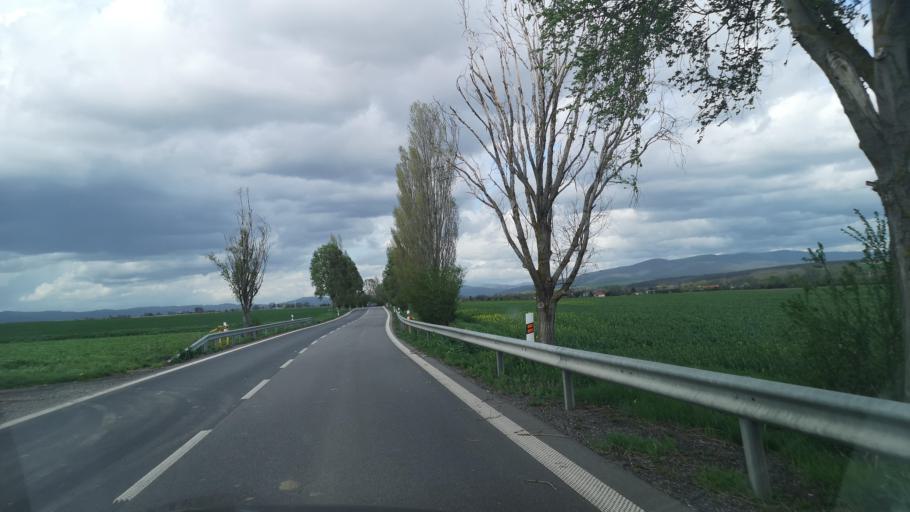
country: SK
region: Nitriansky
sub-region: Okres Nitra
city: Vrable
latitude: 48.3208
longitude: 18.3446
